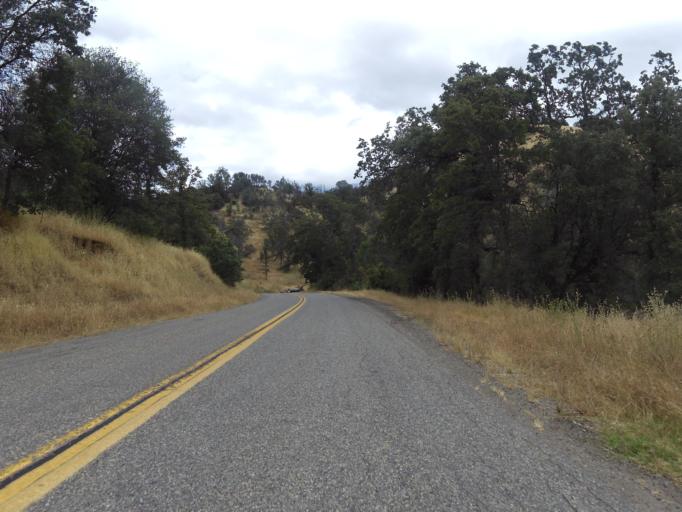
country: US
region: California
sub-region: Madera County
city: Ahwahnee
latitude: 37.3396
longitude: -119.7704
